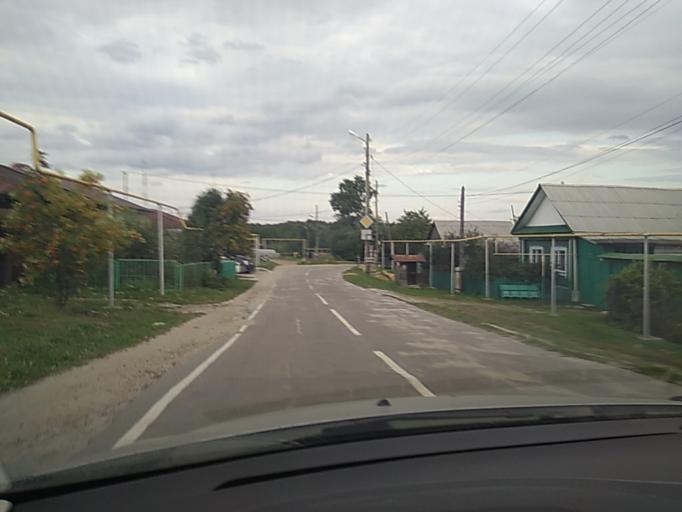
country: RU
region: Chelyabinsk
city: Kyshtym
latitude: 55.6975
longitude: 60.5315
